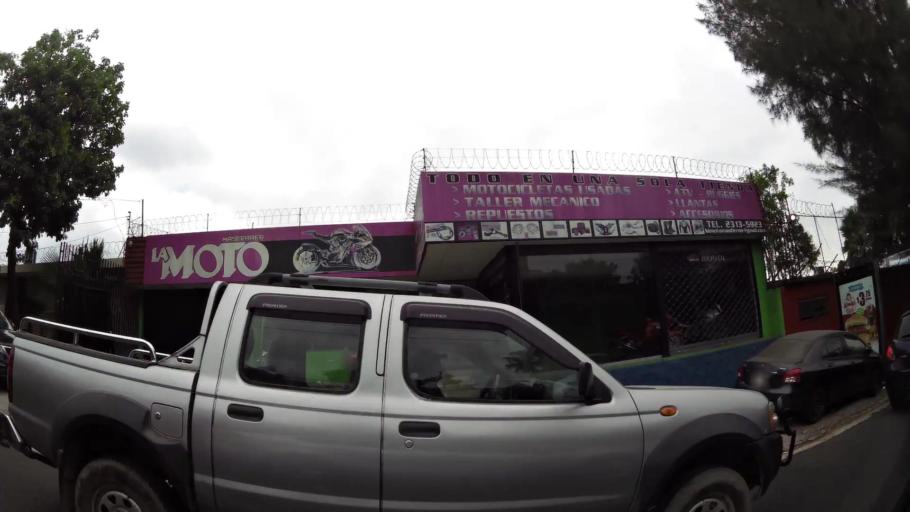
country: SV
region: La Libertad
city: Antiguo Cuscatlan
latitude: 13.7036
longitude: -89.2359
